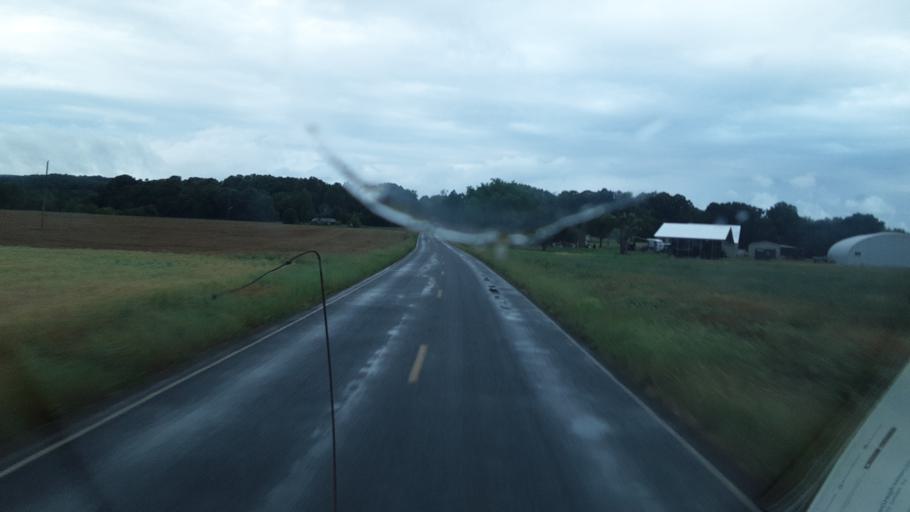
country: US
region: North Carolina
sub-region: Yadkin County
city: Jonesville
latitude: 36.1032
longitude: -80.8762
